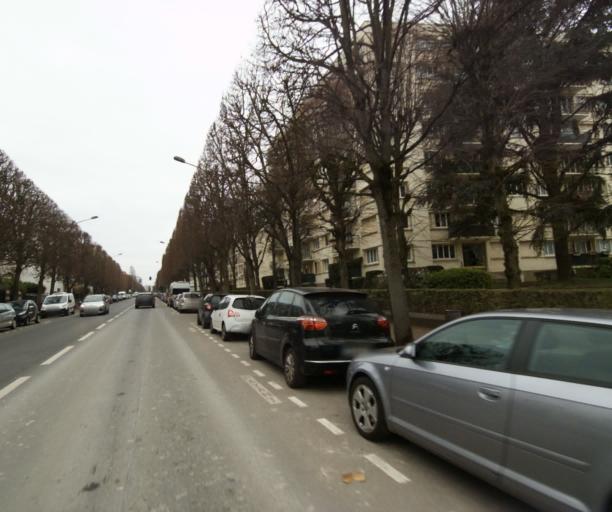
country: FR
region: Ile-de-France
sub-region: Departement des Hauts-de-Seine
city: Saint-Cloud
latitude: 48.8557
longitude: 2.2116
